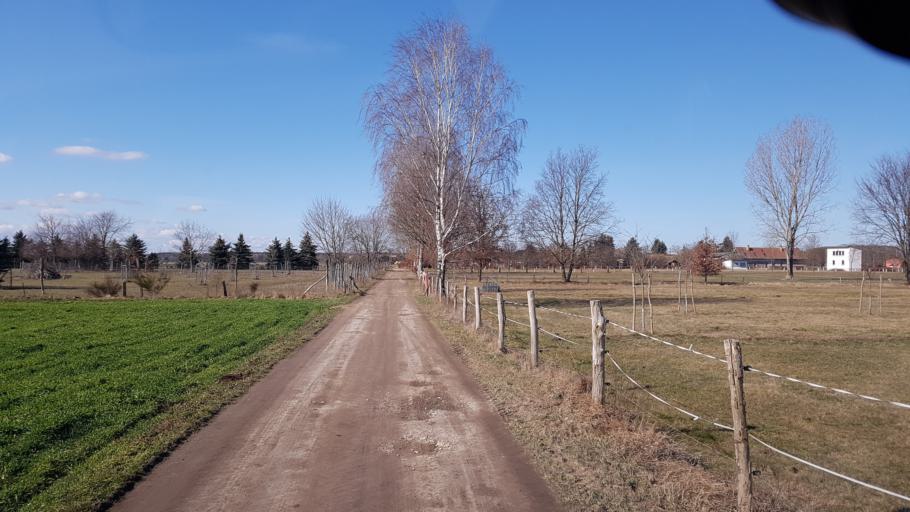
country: DE
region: Brandenburg
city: Schonborn
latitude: 51.5663
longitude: 13.5177
